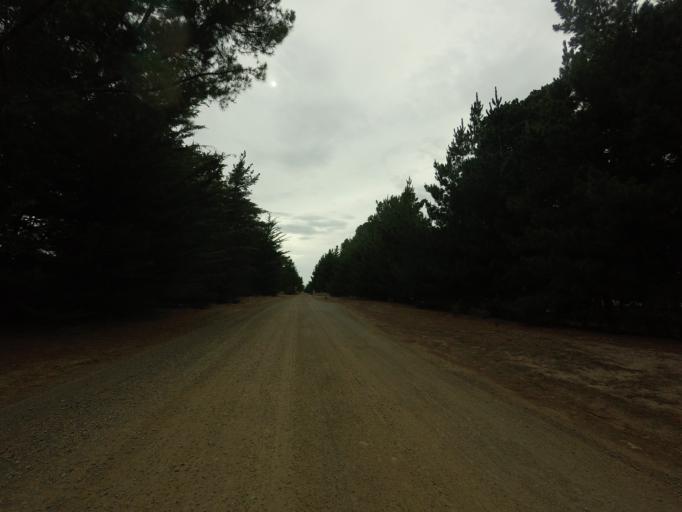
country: AU
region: Tasmania
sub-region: Clarence
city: Seven Mile Beach
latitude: -42.8339
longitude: 147.5375
